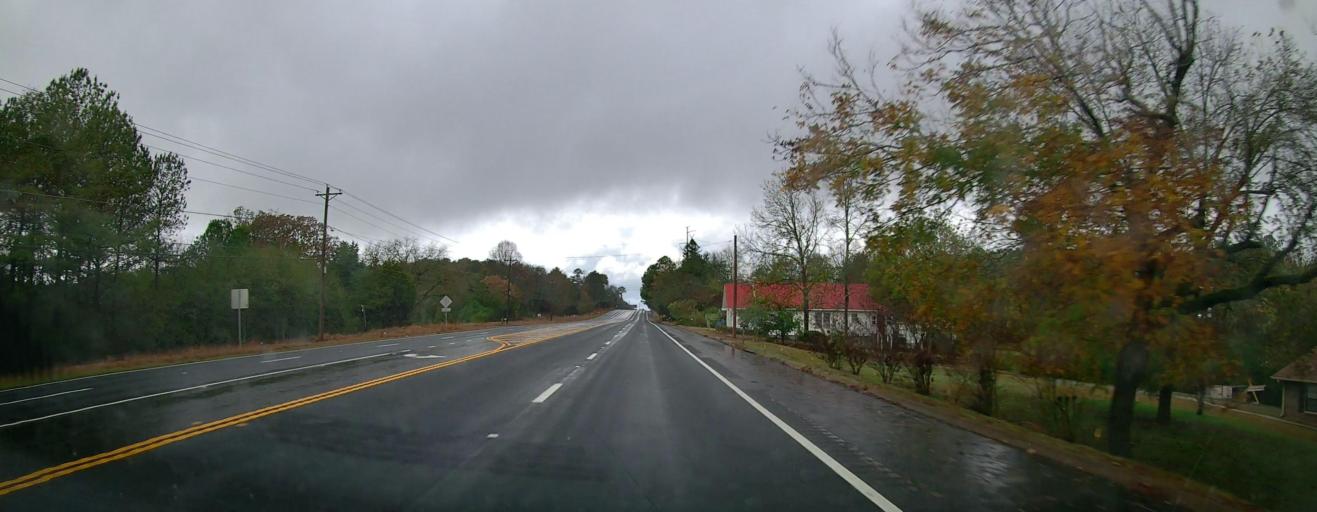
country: US
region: Georgia
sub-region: Clarke County
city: Country Club Estates
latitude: 34.0176
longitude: -83.3909
